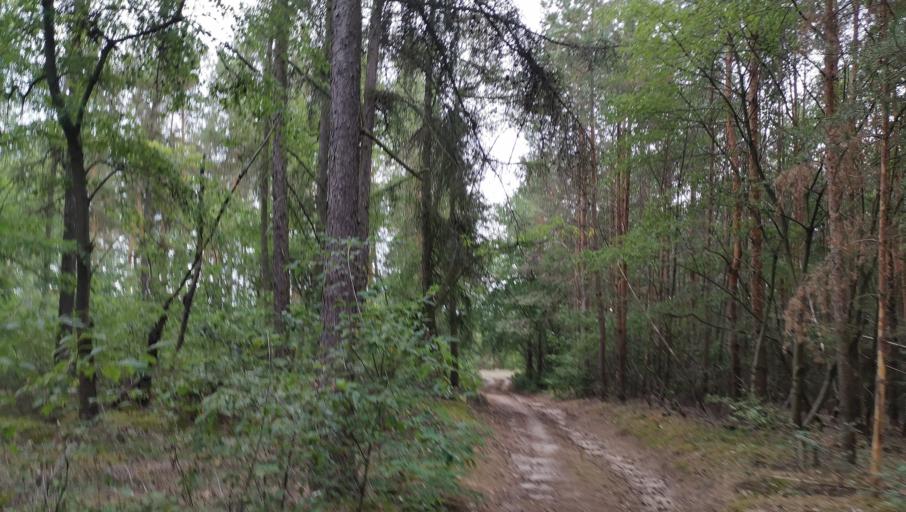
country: DE
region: Brandenburg
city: Potsdam
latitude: 52.3688
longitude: 13.0369
